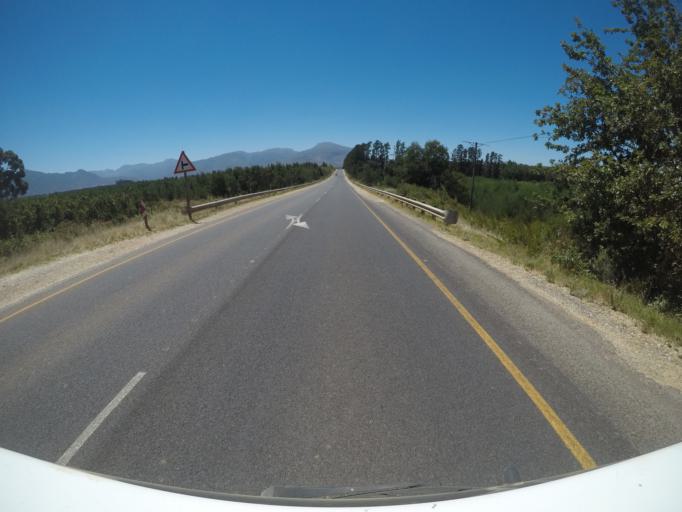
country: ZA
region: Western Cape
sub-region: Overberg District Municipality
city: Grabouw
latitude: -34.0554
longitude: 19.1466
